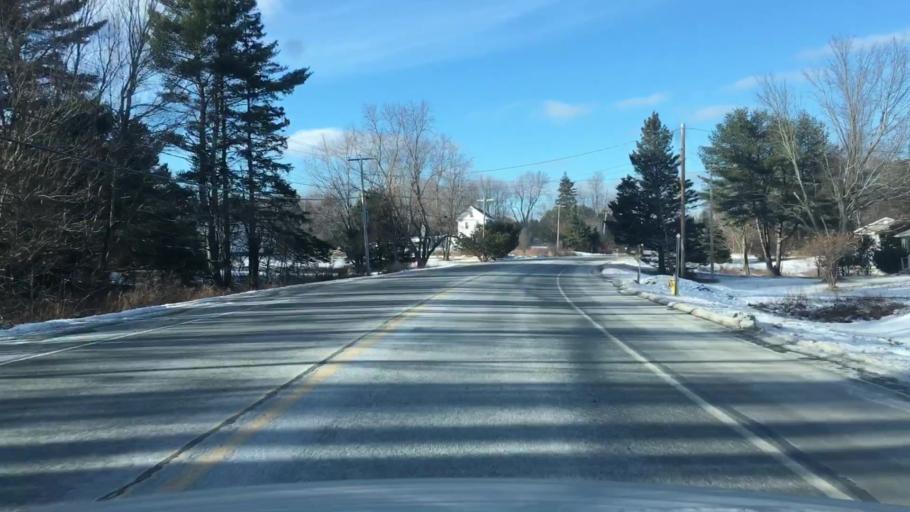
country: US
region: Maine
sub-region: Penobscot County
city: Eddington
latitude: 44.8185
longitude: -68.6468
